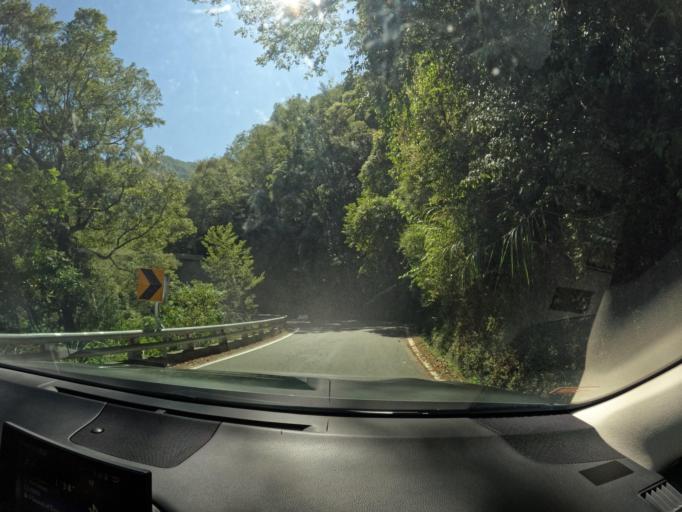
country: TW
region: Taiwan
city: Yujing
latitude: 23.2835
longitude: 120.8723
